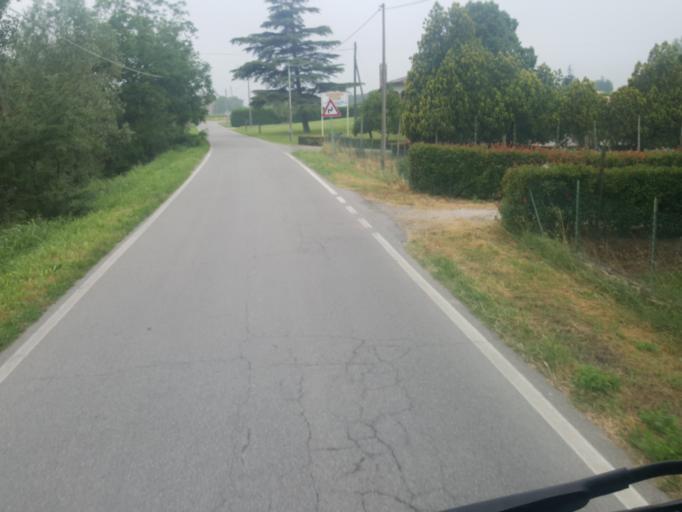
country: IT
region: Veneto
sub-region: Provincia di Rovigo
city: Canaro
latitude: 44.9344
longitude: 11.6539
